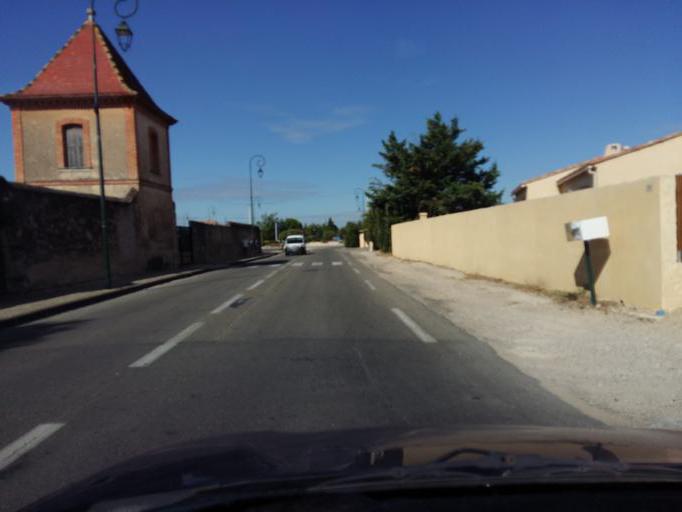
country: FR
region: Provence-Alpes-Cote d'Azur
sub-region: Departement du Vaucluse
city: Mazan
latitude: 44.0580
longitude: 5.1222
